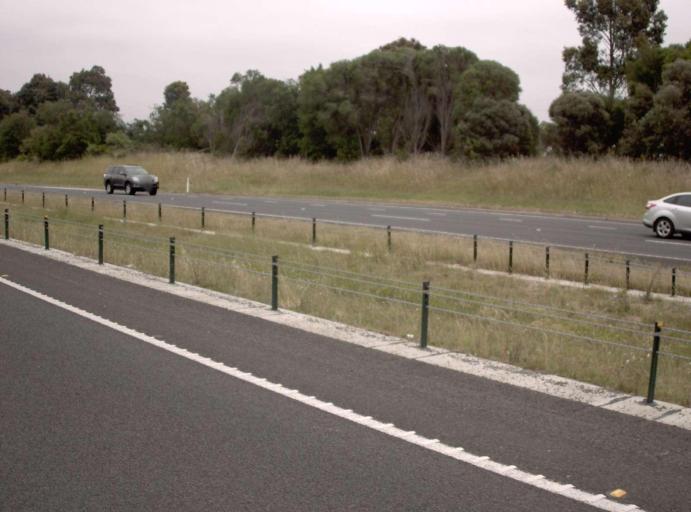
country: AU
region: Victoria
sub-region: Latrobe
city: Morwell
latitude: -38.2426
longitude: 146.4046
